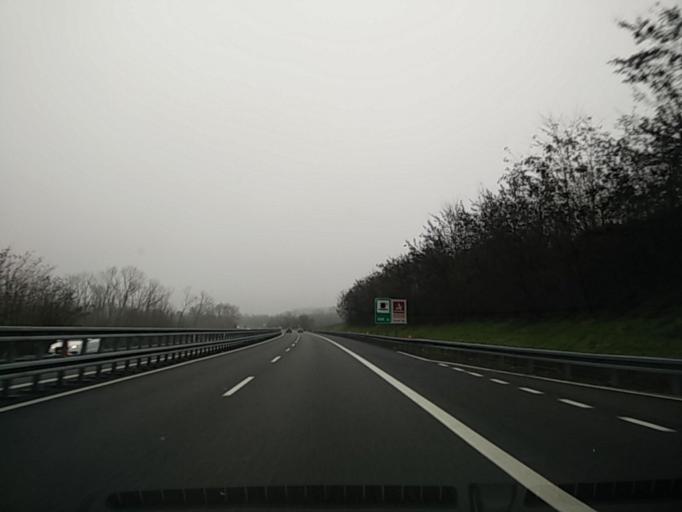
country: IT
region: Piedmont
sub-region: Provincia di Asti
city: Refrancore
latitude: 44.9050
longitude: 8.3425
